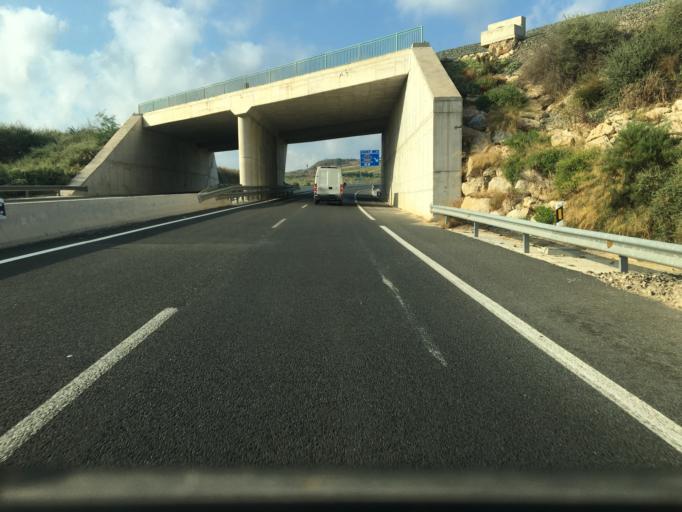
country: ES
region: Murcia
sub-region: Murcia
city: Beniel
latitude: 37.9885
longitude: -0.9740
